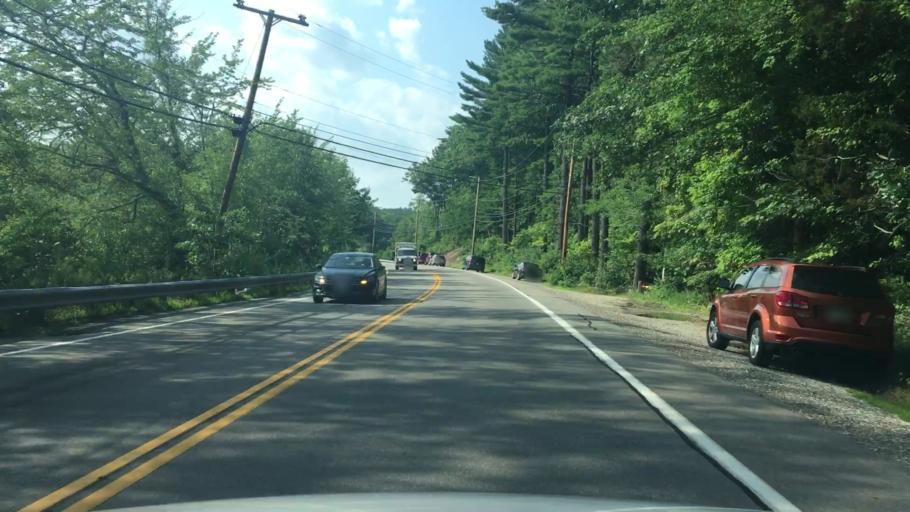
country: US
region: New Hampshire
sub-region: Rockingham County
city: Auburn
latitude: 42.9861
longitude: -71.3740
